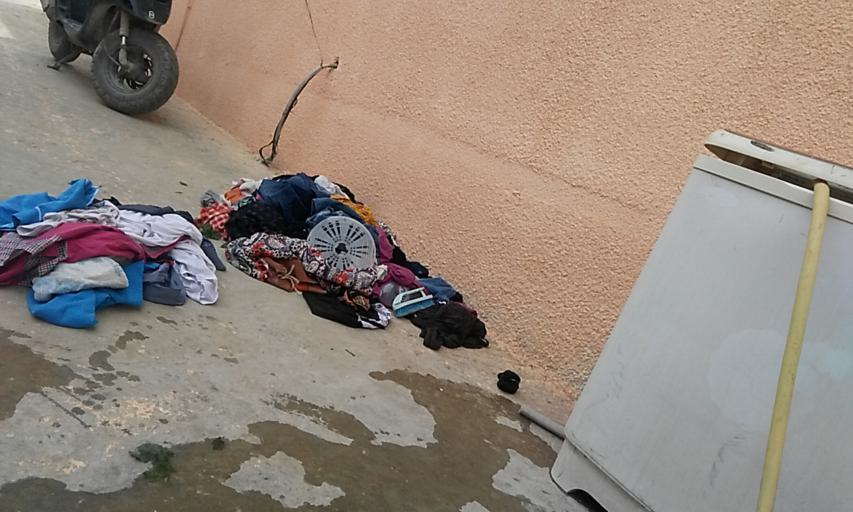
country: TN
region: Banzart
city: Menzel Bourguiba
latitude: 37.1358
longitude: 9.7725
